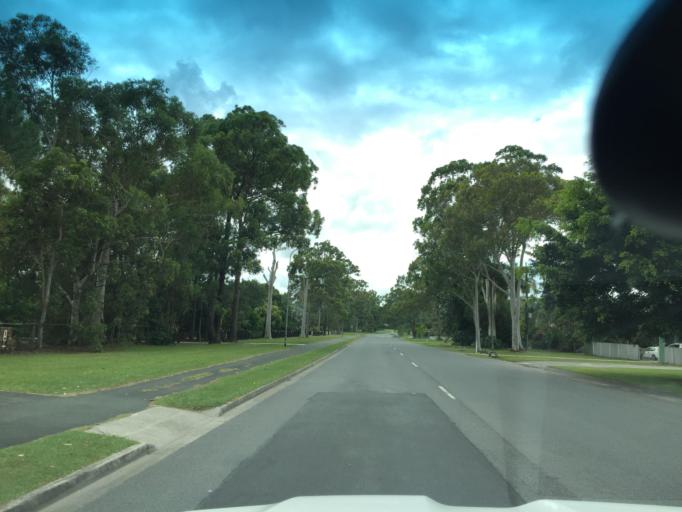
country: AU
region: Queensland
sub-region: Moreton Bay
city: Burpengary
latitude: -27.1309
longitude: 152.9856
